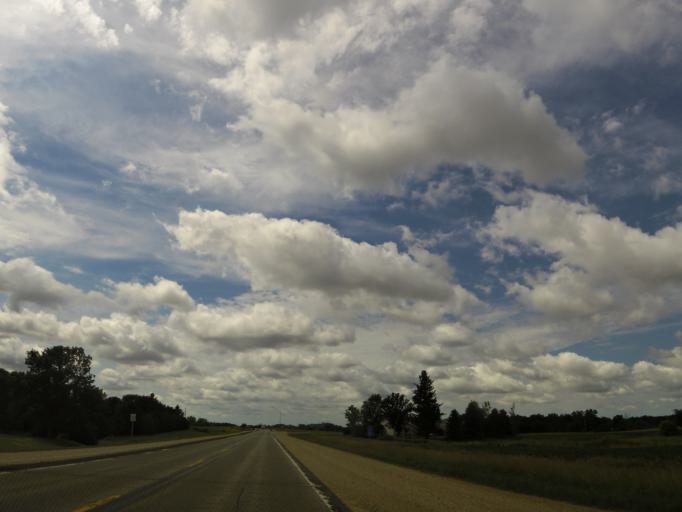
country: US
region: Iowa
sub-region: Chickasaw County
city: New Hampton
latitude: 43.2514
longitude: -92.2985
